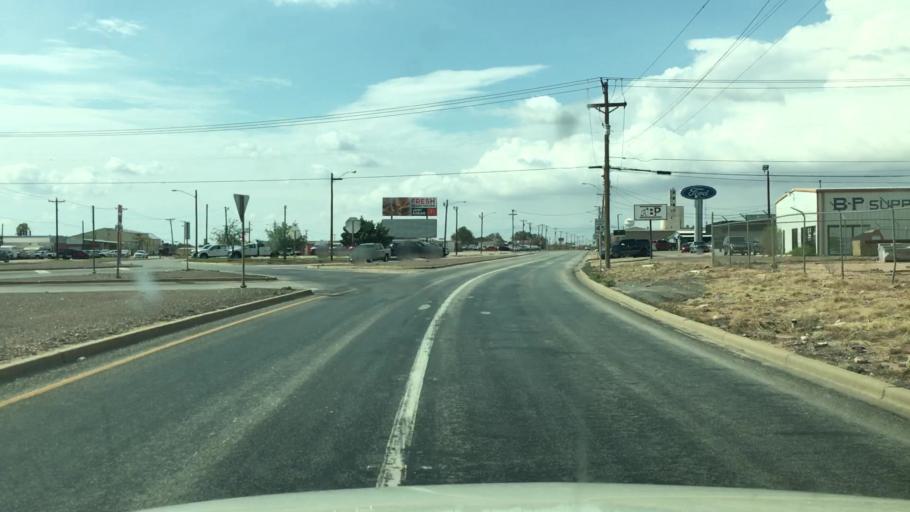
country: US
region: Texas
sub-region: Dawson County
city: Lamesa
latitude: 32.7201
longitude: -101.9450
